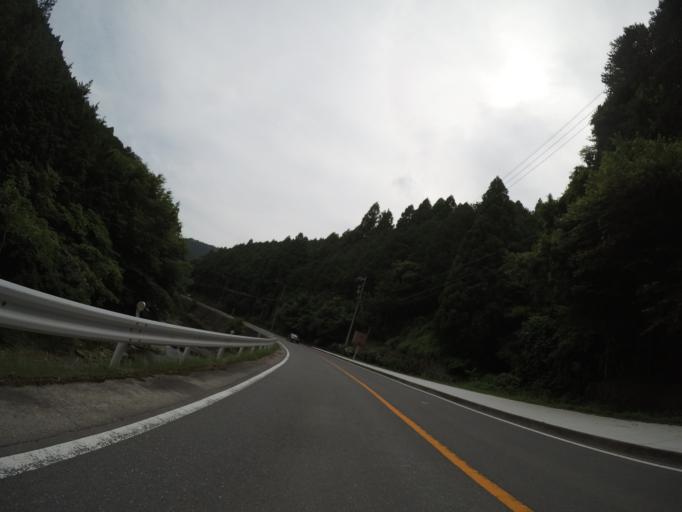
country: JP
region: Shizuoka
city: Fujinomiya
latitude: 35.2008
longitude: 138.5400
